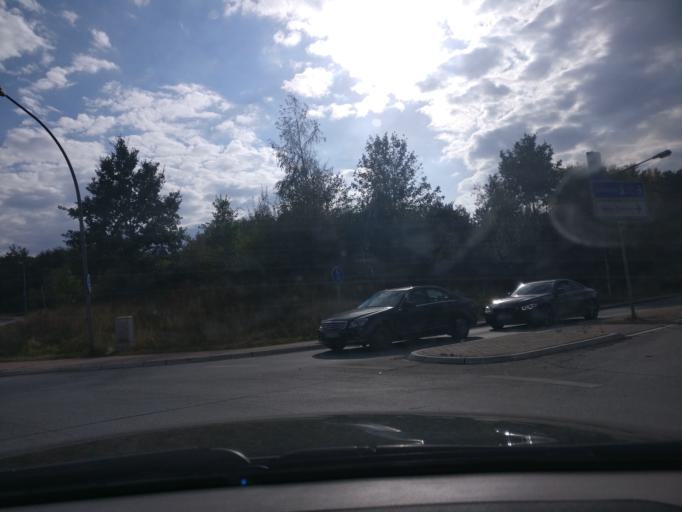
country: DE
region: Lower Saxony
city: Melle
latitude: 52.1926
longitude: 8.3467
